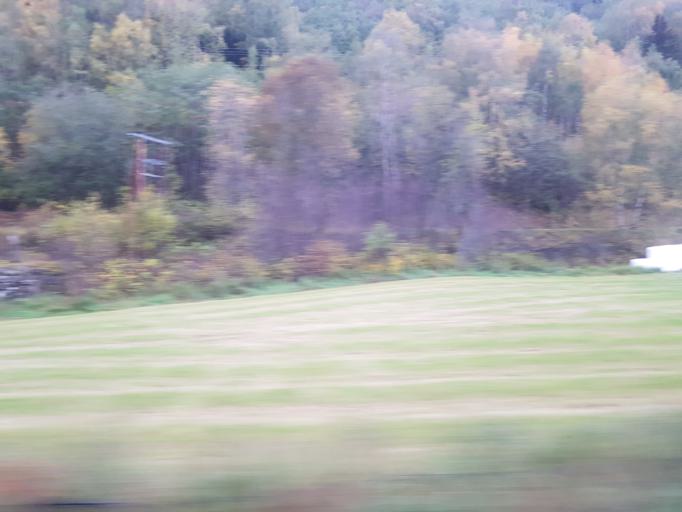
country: NO
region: Oppland
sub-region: Sel
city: Otta
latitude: 61.7796
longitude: 9.5375
